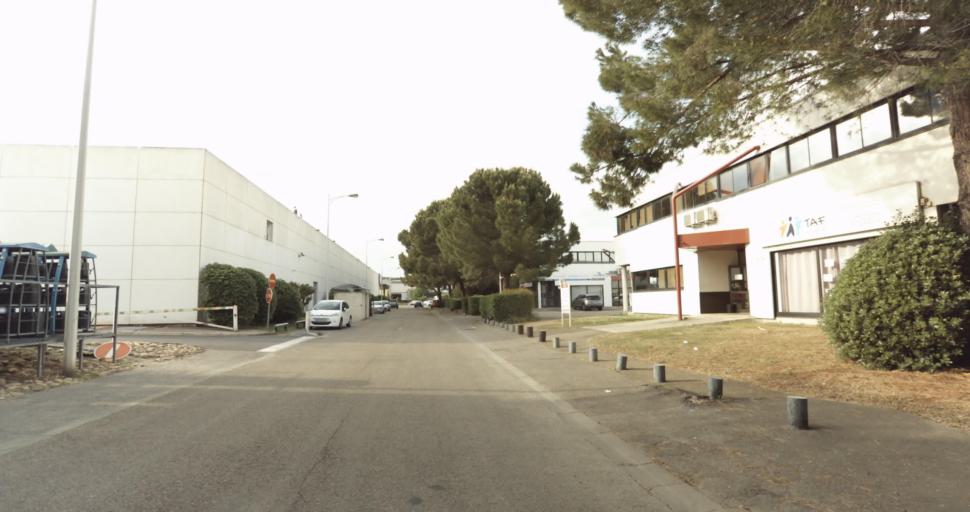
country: FR
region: Languedoc-Roussillon
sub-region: Departement du Gard
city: Nimes
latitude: 43.8129
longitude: 4.3515
